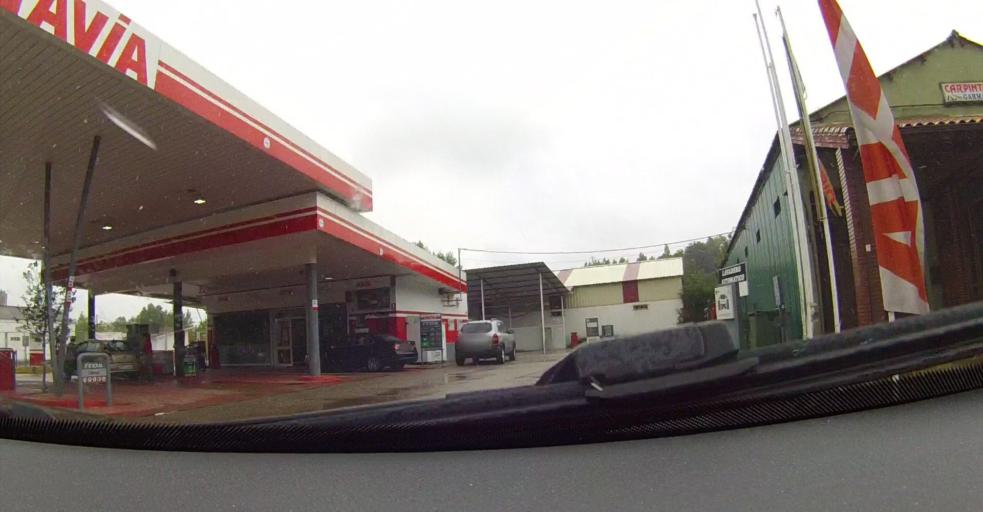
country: ES
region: Castille and Leon
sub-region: Provincia de Palencia
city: Guardo
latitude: 42.7988
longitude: -4.8483
